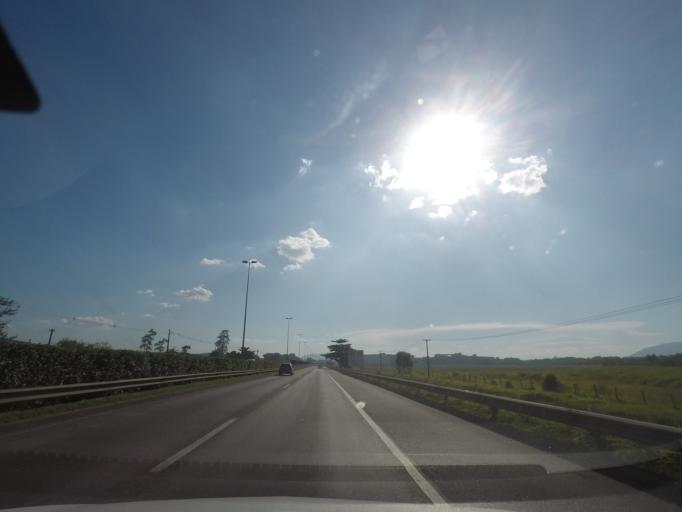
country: BR
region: Rio de Janeiro
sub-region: Duque De Caxias
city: Duque de Caxias
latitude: -22.6616
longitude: -43.2543
